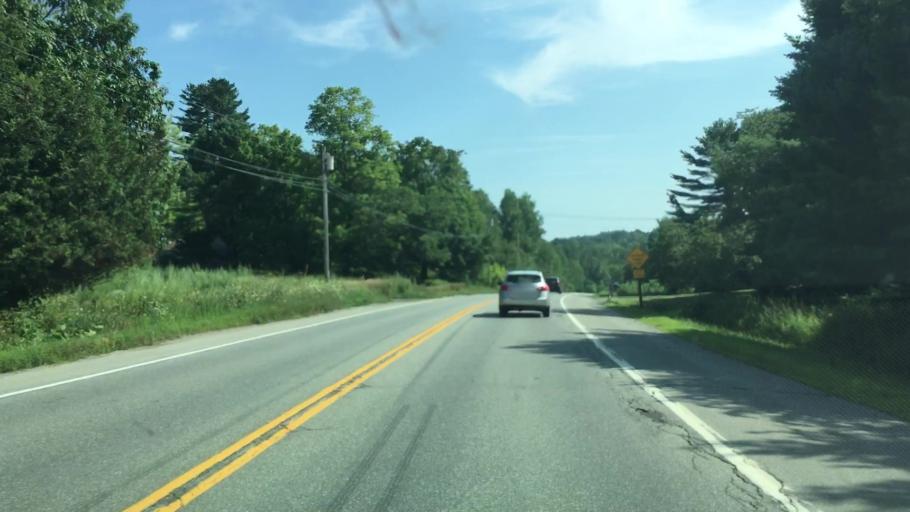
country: US
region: Maine
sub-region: Penobscot County
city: Orrington
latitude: 44.7029
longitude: -68.8445
